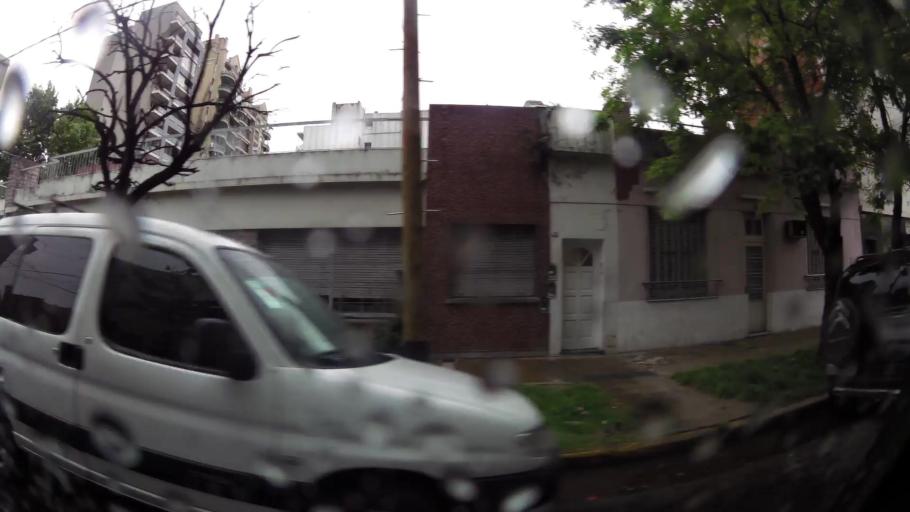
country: AR
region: Buenos Aires
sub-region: Partido de Lanus
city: Lanus
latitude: -34.7066
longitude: -58.3960
